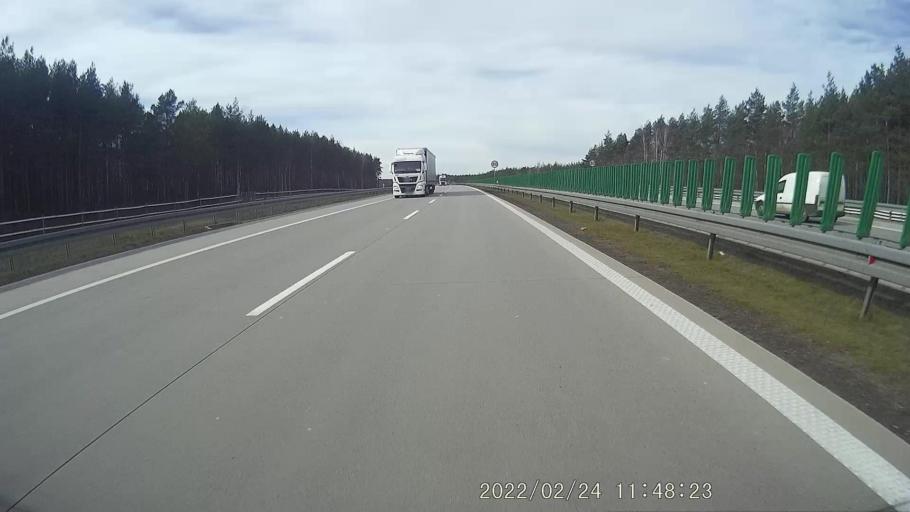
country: PL
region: Lower Silesian Voivodeship
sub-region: Powiat polkowicki
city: Radwanice
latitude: 51.5829
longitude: 15.9554
